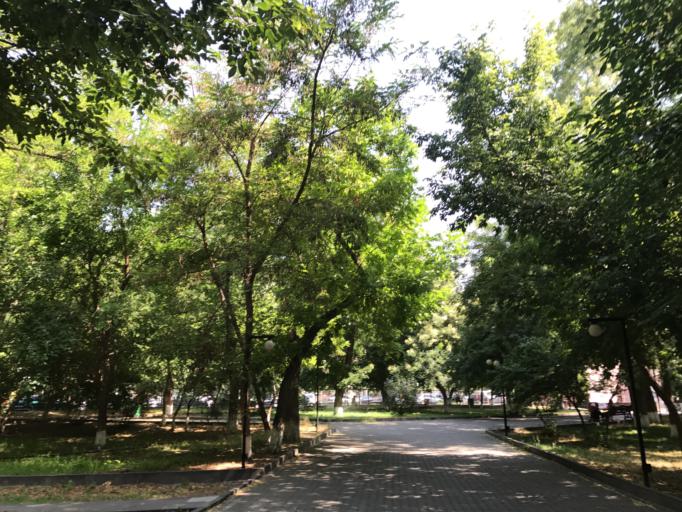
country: AM
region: Yerevan
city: Yerevan
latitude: 40.1760
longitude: 44.5060
